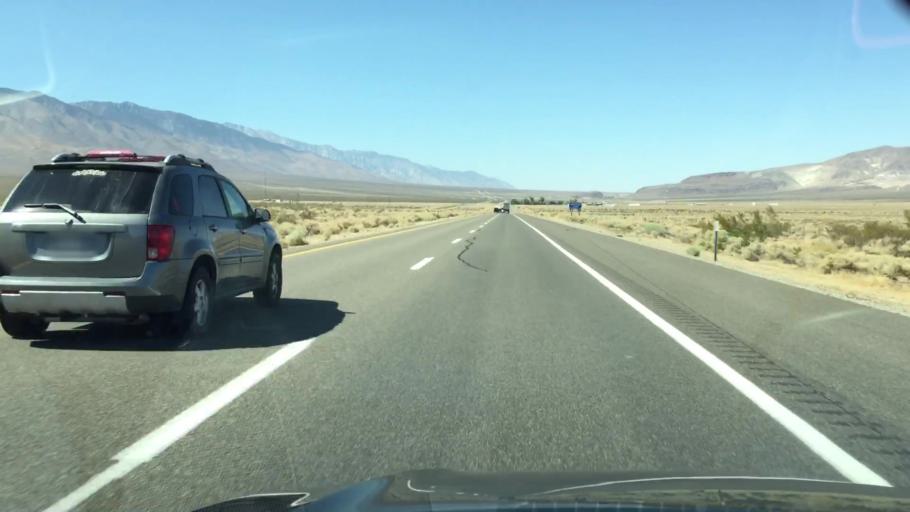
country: US
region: California
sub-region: Kern County
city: Inyokern
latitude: 36.0309
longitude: -117.9424
